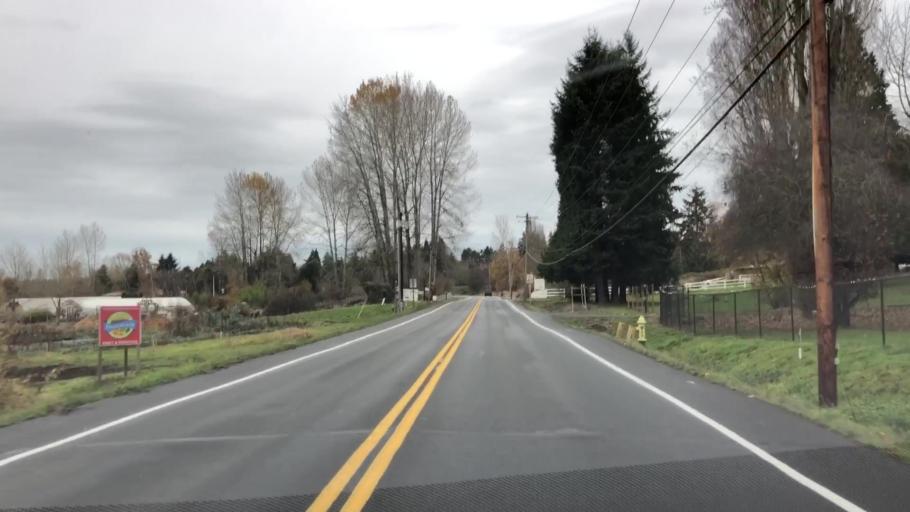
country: US
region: Washington
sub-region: King County
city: Woodinville
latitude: 47.7445
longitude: -122.1474
